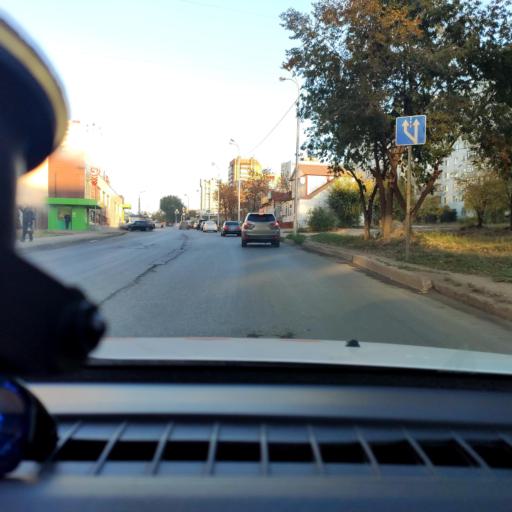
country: RU
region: Samara
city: Samara
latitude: 53.1900
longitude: 50.1433
